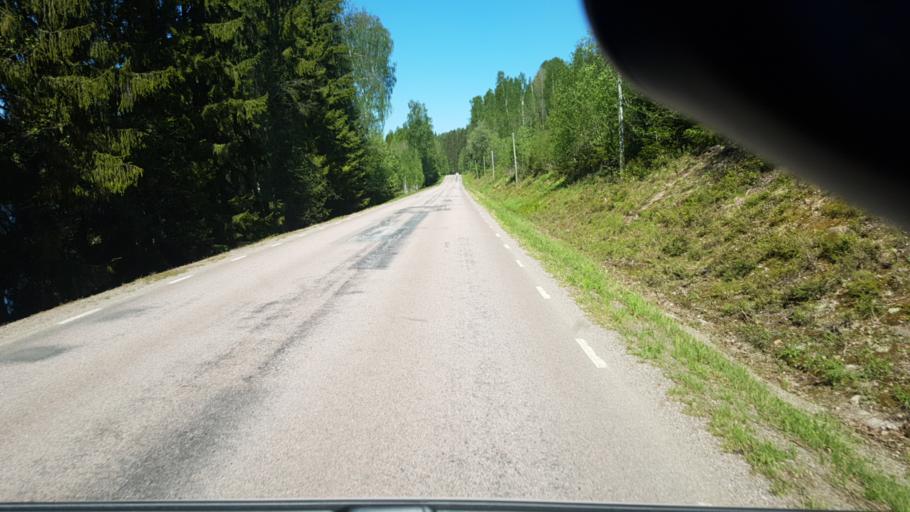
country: SE
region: Vaermland
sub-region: Eda Kommun
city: Amotfors
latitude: 59.8951
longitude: 12.5252
